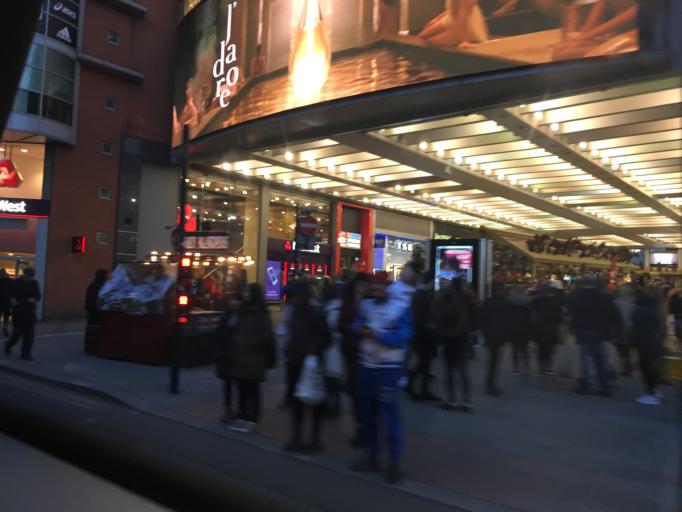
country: GB
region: England
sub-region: Manchester
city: Manchester
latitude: 53.4828
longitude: -2.2437
